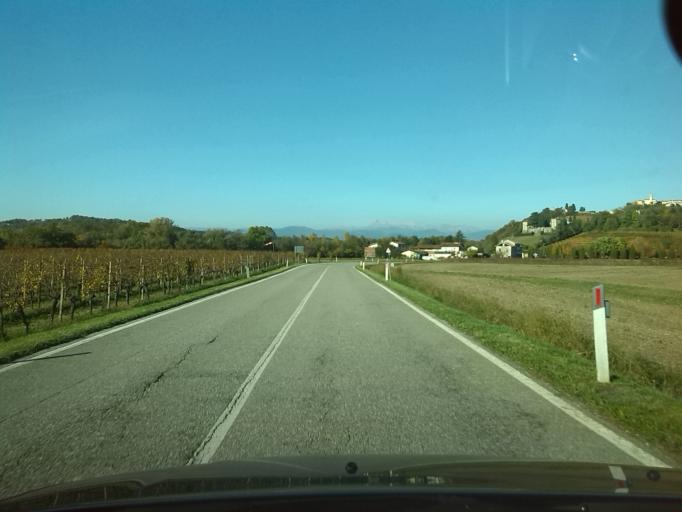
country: IT
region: Friuli Venezia Giulia
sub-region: Provincia di Udine
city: Corno di Rosazzo
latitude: 45.9854
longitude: 13.4672
